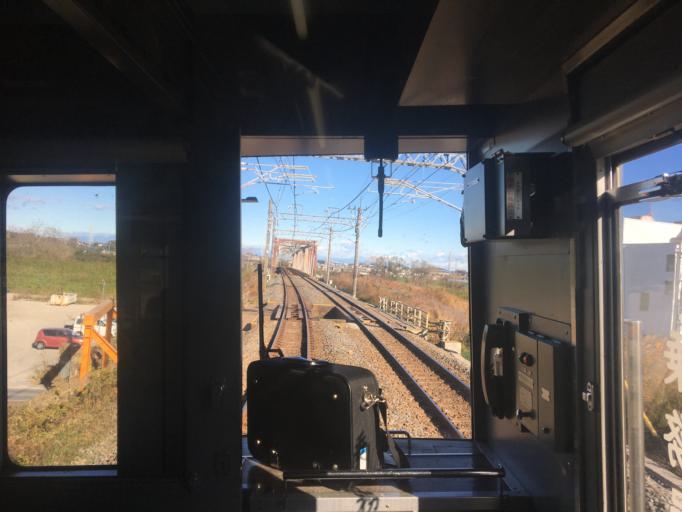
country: JP
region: Saitama
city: Sakado
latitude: 35.9833
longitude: 139.4006
